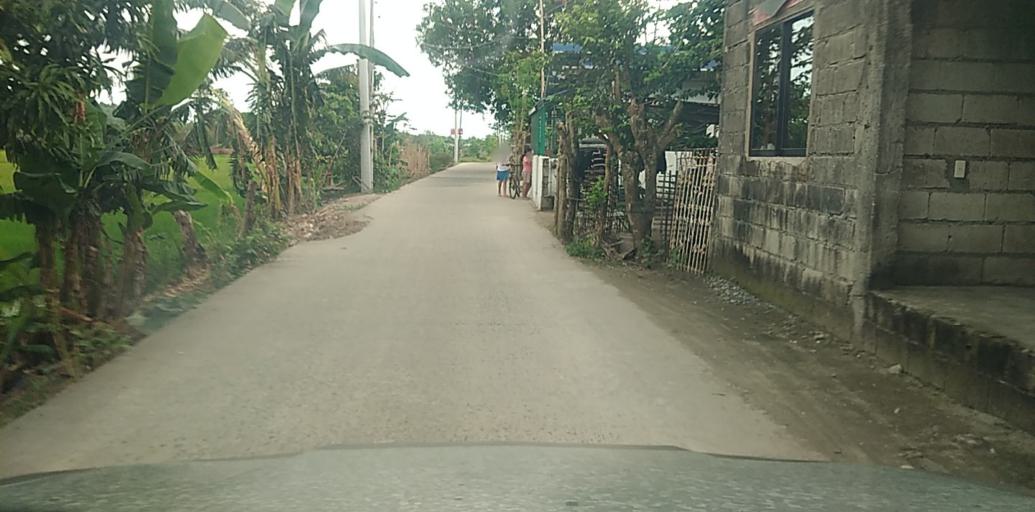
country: PH
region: Central Luzon
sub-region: Province of Pampanga
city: Panlinlang
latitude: 15.1800
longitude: 120.7001
